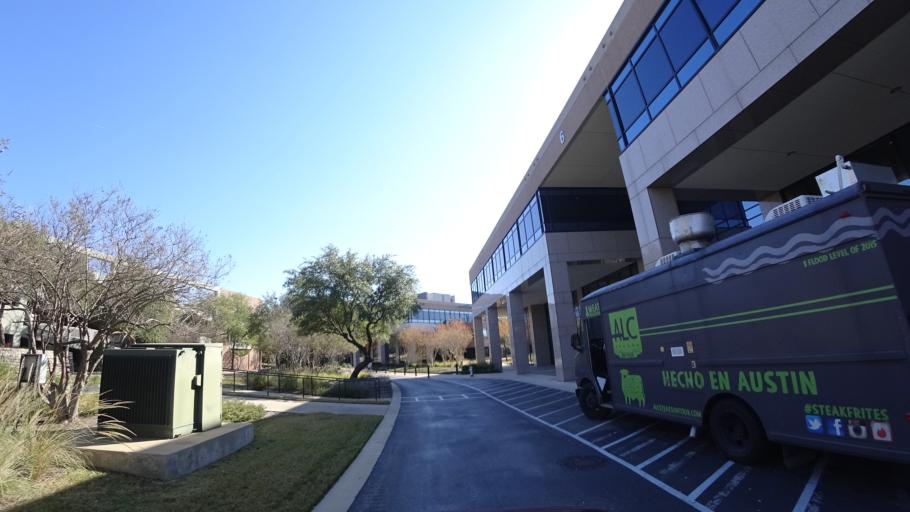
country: US
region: Texas
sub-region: Williamson County
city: Anderson Mill
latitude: 30.3960
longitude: -97.8515
